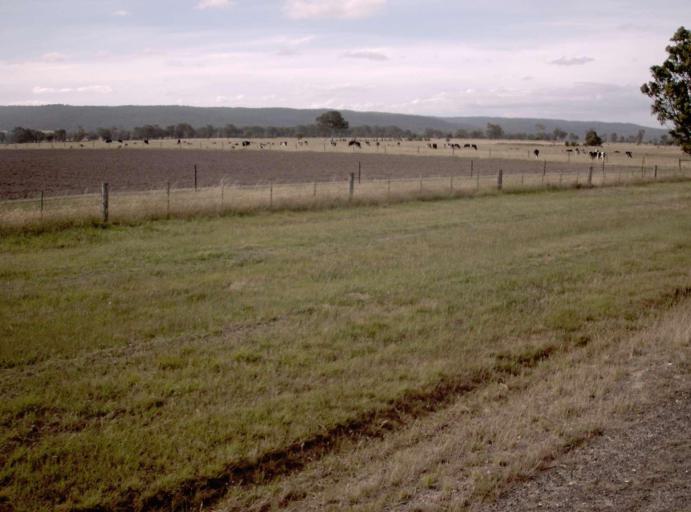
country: AU
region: Victoria
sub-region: Wellington
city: Heyfield
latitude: -38.0453
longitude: 146.6649
